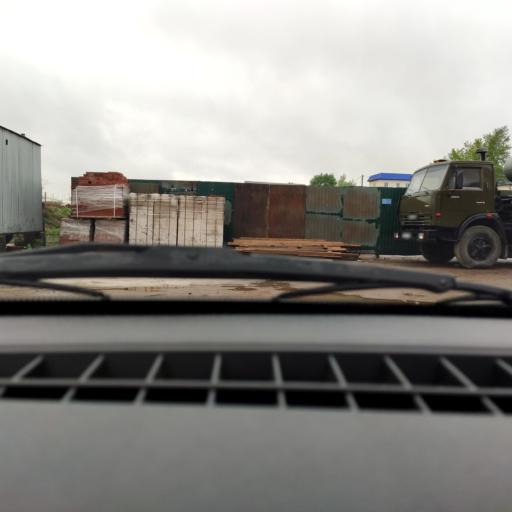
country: RU
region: Bashkortostan
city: Ufa
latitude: 54.7674
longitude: 55.9644
